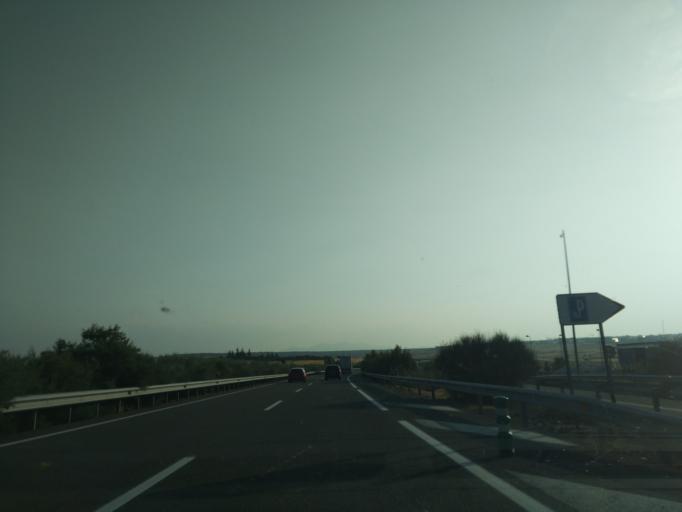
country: ES
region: Castille and Leon
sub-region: Provincia de Avila
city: Berrocalejo de Aragona
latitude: 40.6912
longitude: -4.5869
